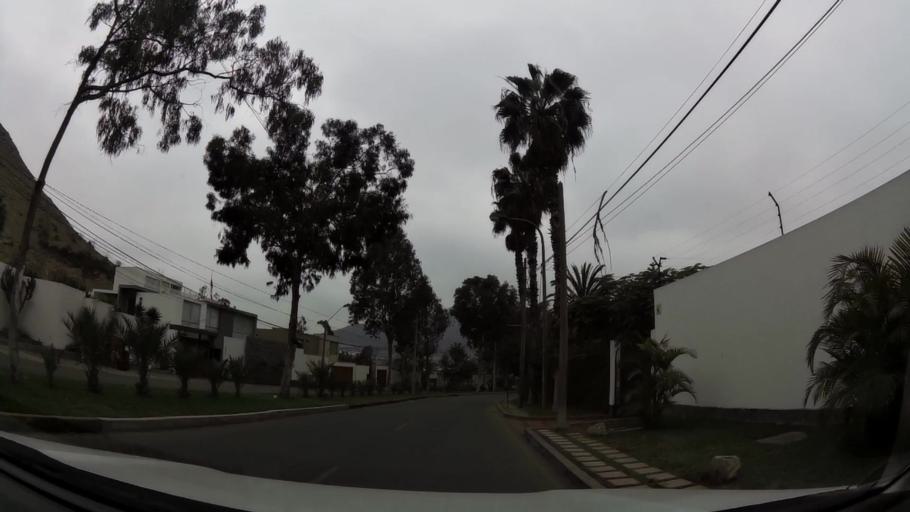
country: PE
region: Lima
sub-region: Lima
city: La Molina
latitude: -12.0906
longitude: -76.9263
